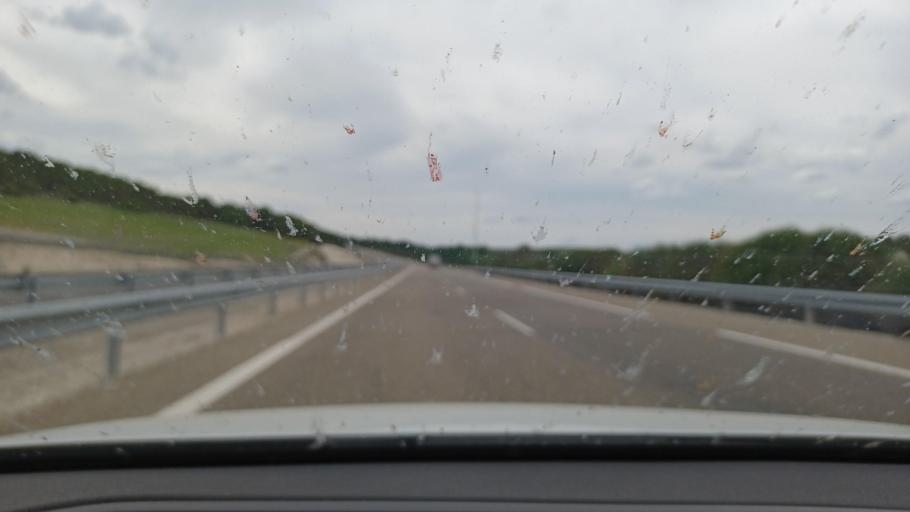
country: ES
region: Castille and Leon
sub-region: Provincia de Valladolid
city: Viloria
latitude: 41.4431
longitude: -4.4080
